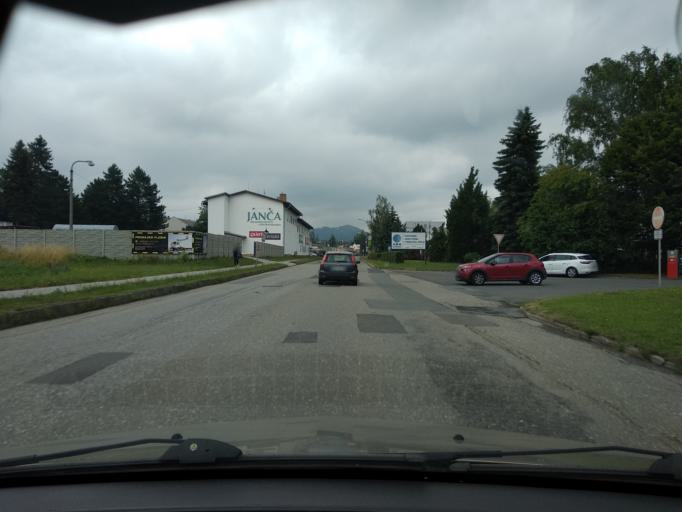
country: CZ
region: Olomoucky
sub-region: Okres Sumperk
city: Sumperk
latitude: 49.9539
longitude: 16.9608
